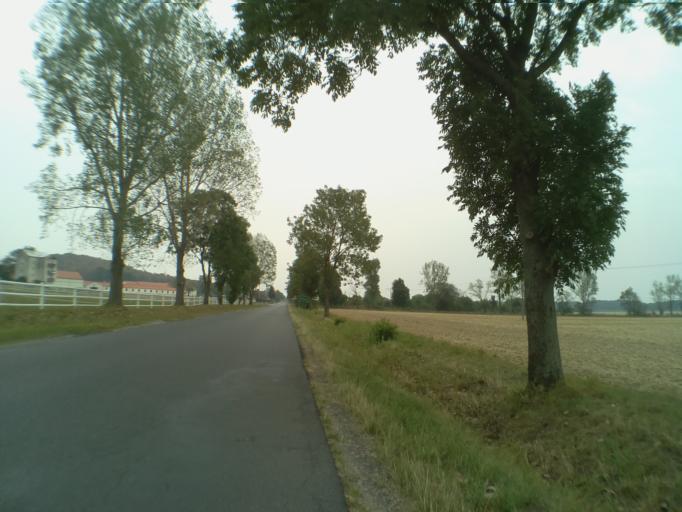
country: PL
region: Lower Silesian Voivodeship
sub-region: Powiat swidnicki
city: Strzegom
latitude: 50.9777
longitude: 16.2827
